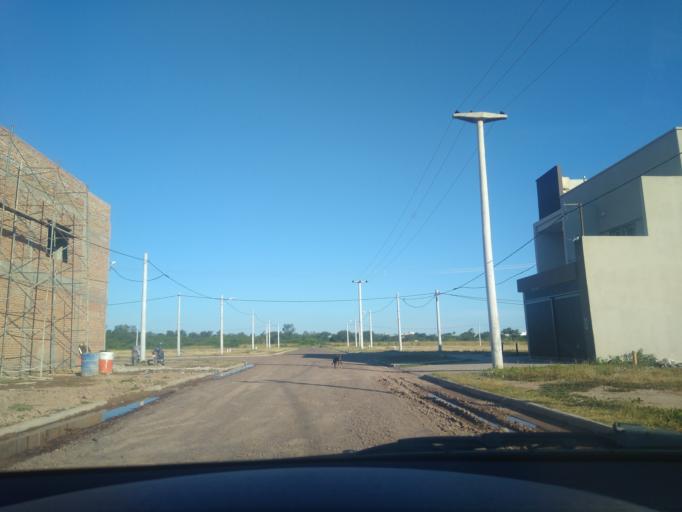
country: AR
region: Chaco
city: Resistencia
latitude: -27.4142
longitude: -58.9585
